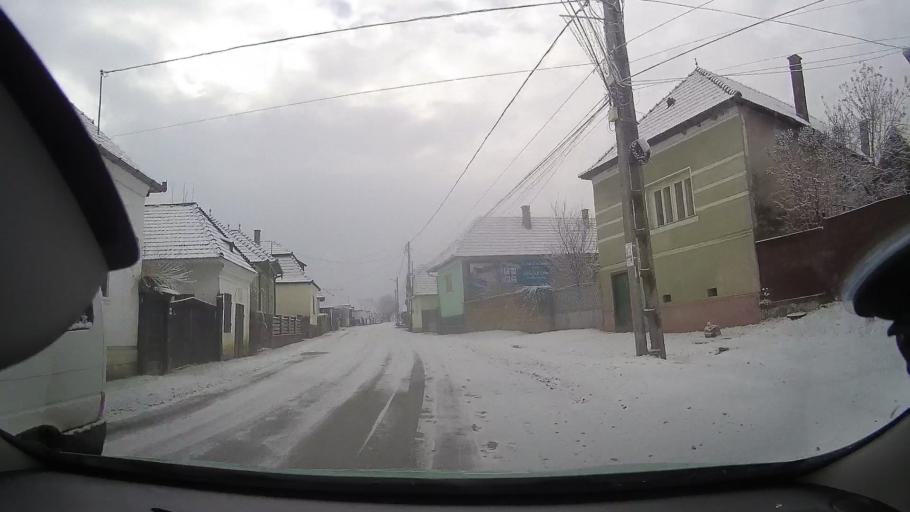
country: RO
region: Alba
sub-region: Comuna Rimetea
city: Rimetea
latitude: 46.4551
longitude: 23.5683
